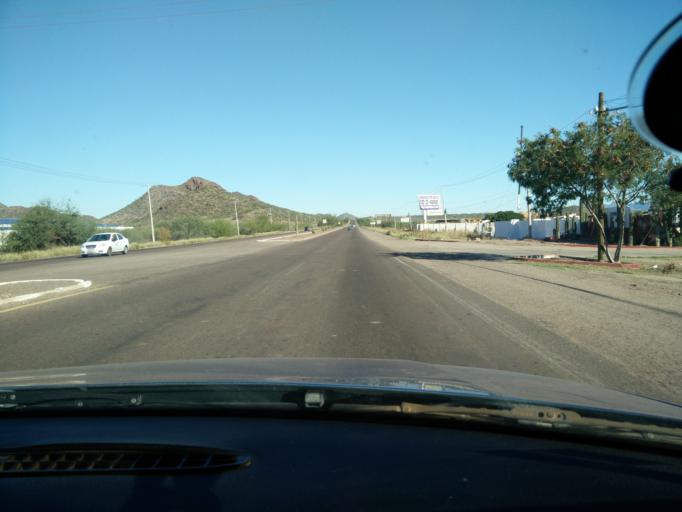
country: MX
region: Sonora
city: Heroica Guaymas
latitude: 27.9621
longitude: -110.9358
